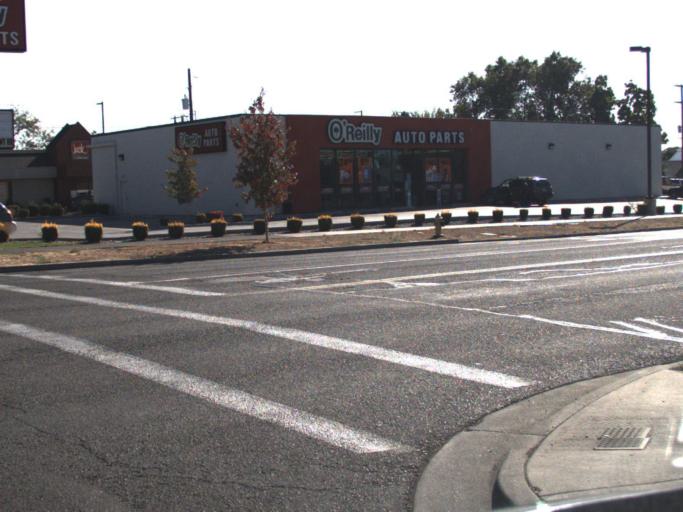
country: US
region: Washington
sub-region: Walla Walla County
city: Walla Walla
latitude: 46.0614
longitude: -118.3471
